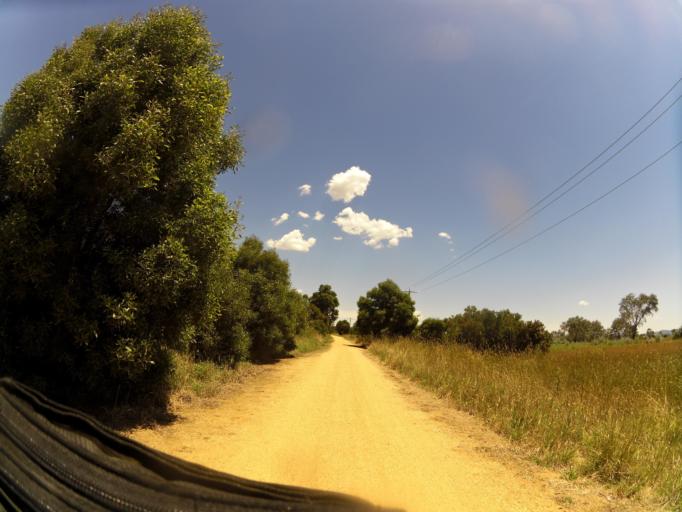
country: AU
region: Victoria
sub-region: Wellington
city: Heyfield
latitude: -37.9662
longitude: 146.9180
